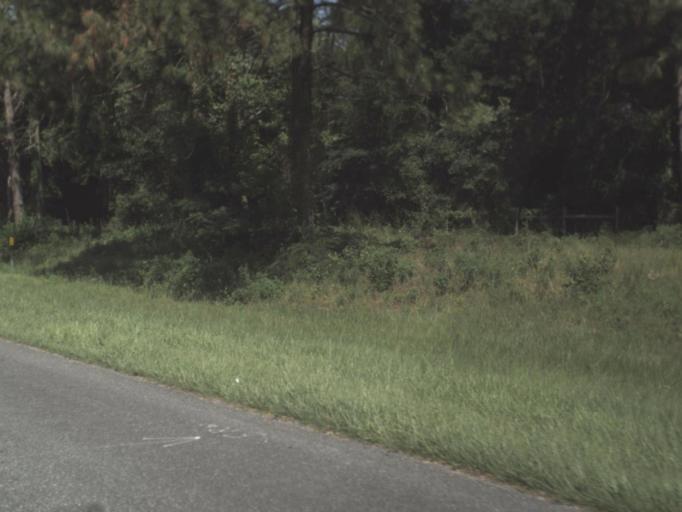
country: US
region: Florida
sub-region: Suwannee County
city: Live Oak
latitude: 30.3384
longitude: -83.0999
